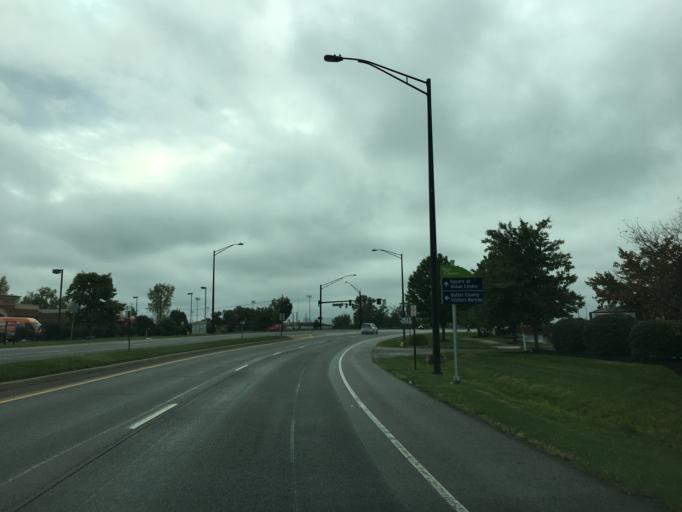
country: US
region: Ohio
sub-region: Butler County
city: Beckett Ridge
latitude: 39.3365
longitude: -84.4364
